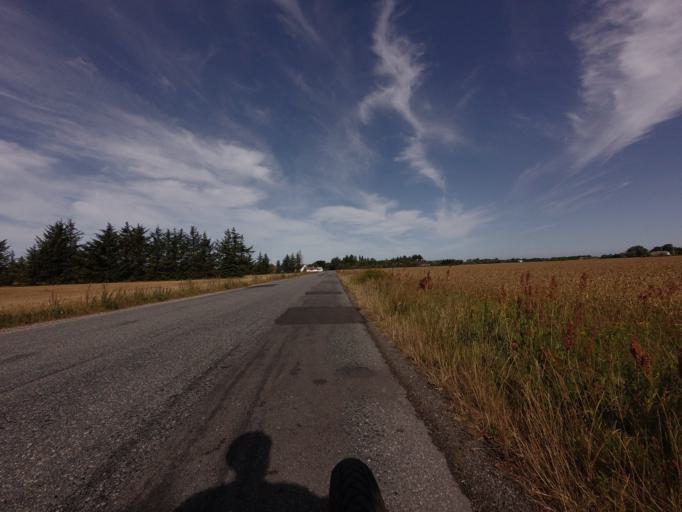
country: DK
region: North Denmark
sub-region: Hjorring Kommune
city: Vra
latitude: 57.4218
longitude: 9.8534
